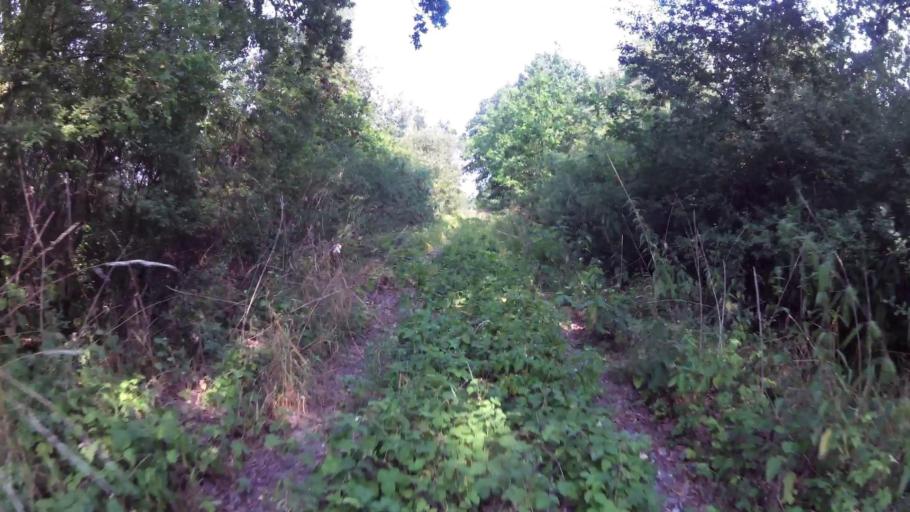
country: PL
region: West Pomeranian Voivodeship
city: Trzcinsko Zdroj
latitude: 52.9137
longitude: 14.5486
